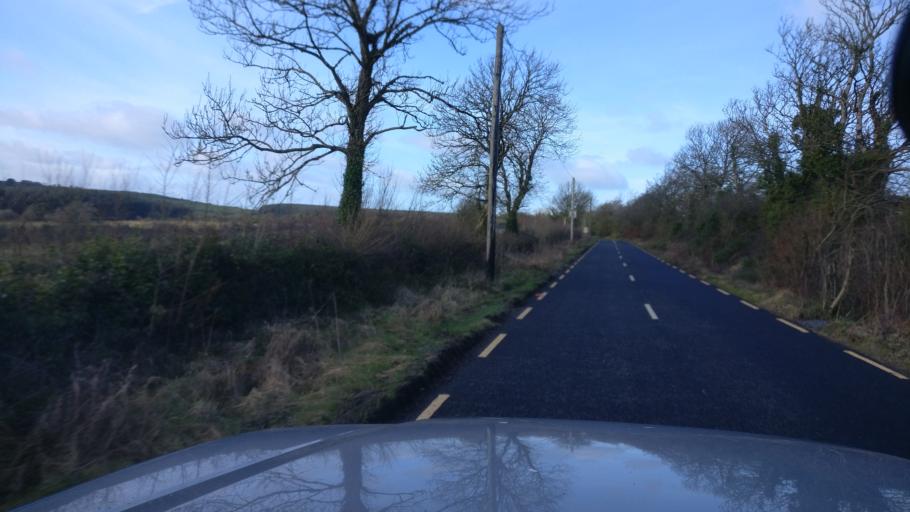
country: IE
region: Leinster
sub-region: Kilkenny
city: Castlecomer
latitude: 52.9006
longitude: -7.1759
